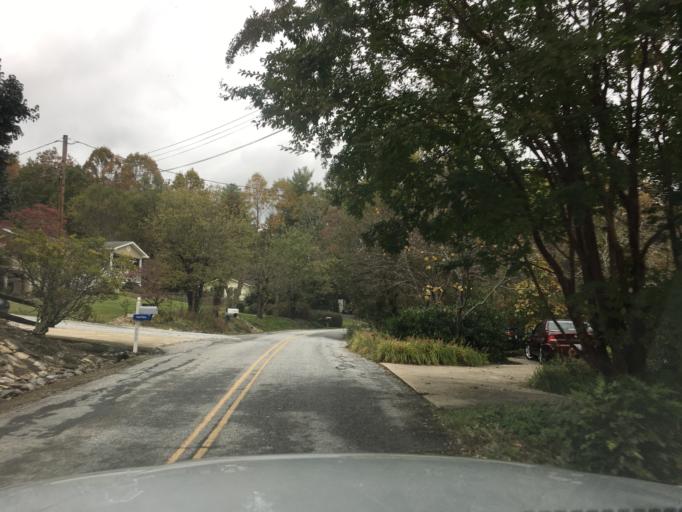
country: US
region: North Carolina
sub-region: Henderson County
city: Valley Hill
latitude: 35.2988
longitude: -82.4860
